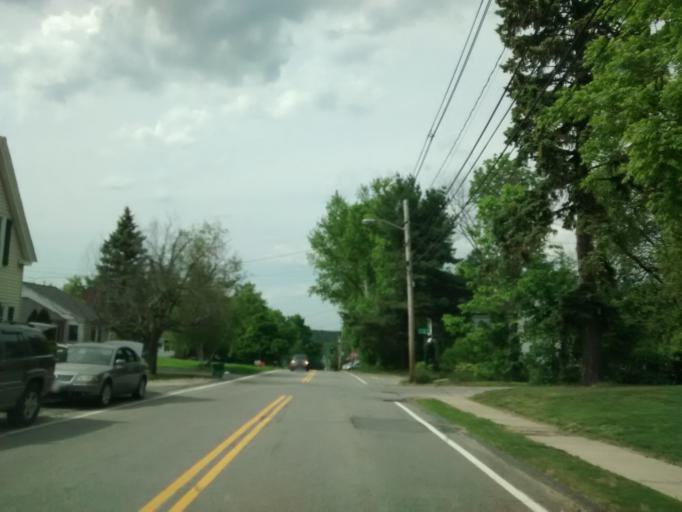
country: US
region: Massachusetts
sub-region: Middlesex County
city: Hopkinton
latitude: 42.2301
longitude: -71.5225
